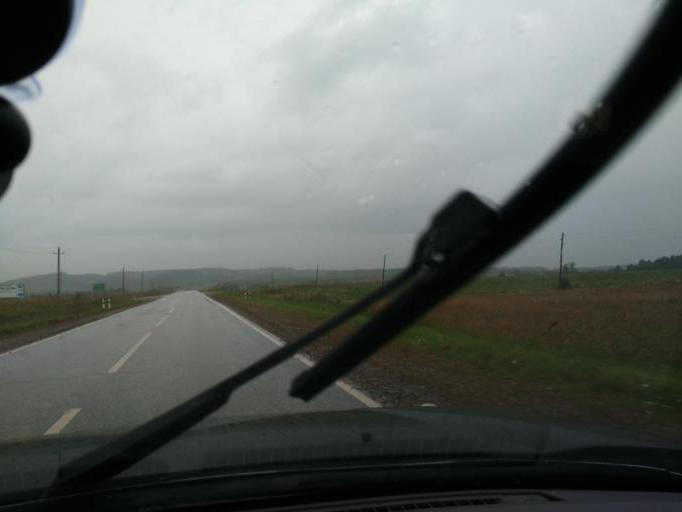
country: RU
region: Perm
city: Barda
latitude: 57.1004
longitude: 55.5295
